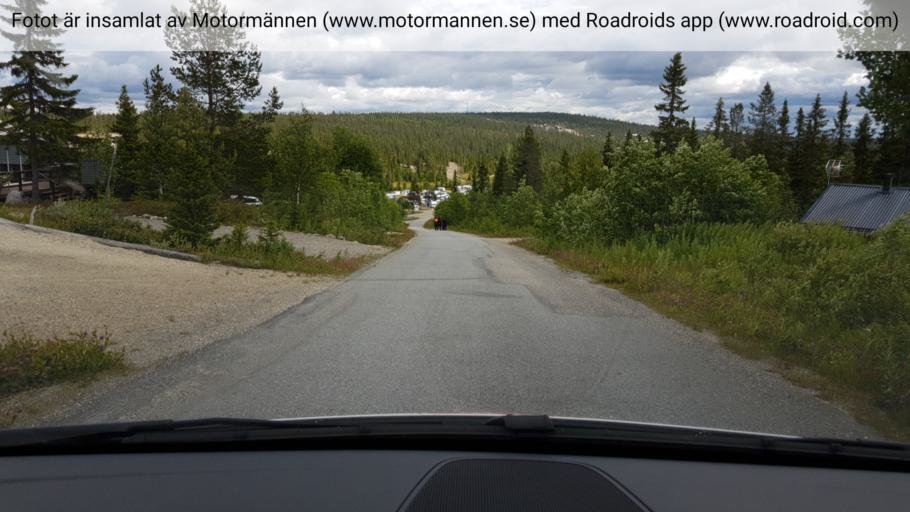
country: SE
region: Jaemtland
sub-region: Bergs Kommun
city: Hoverberg
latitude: 62.5027
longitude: 14.1022
